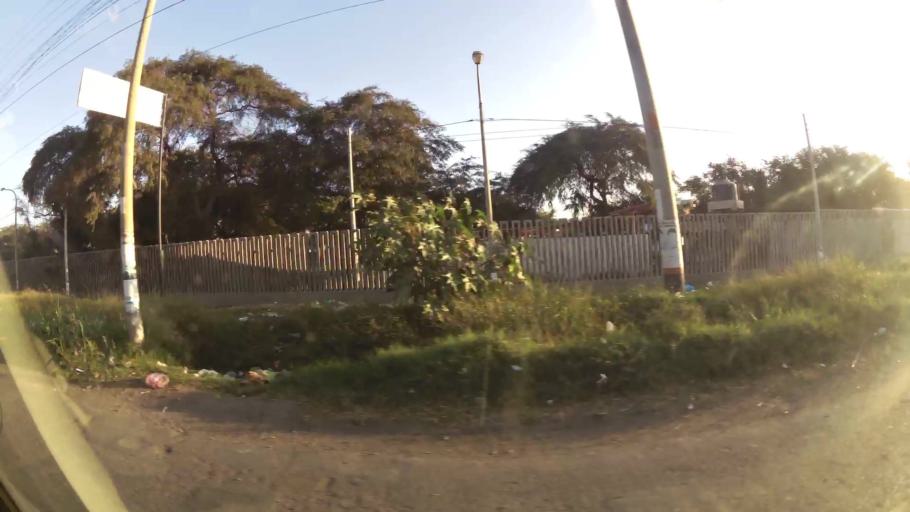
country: PE
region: Ica
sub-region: Provincia de Ica
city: Ica
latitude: -14.0835
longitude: -75.7331
